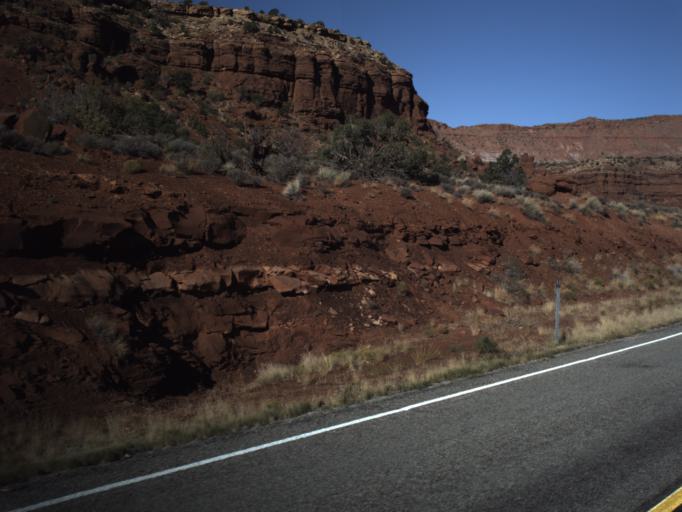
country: US
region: Utah
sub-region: San Juan County
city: Blanding
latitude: 37.6902
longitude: -110.2252
